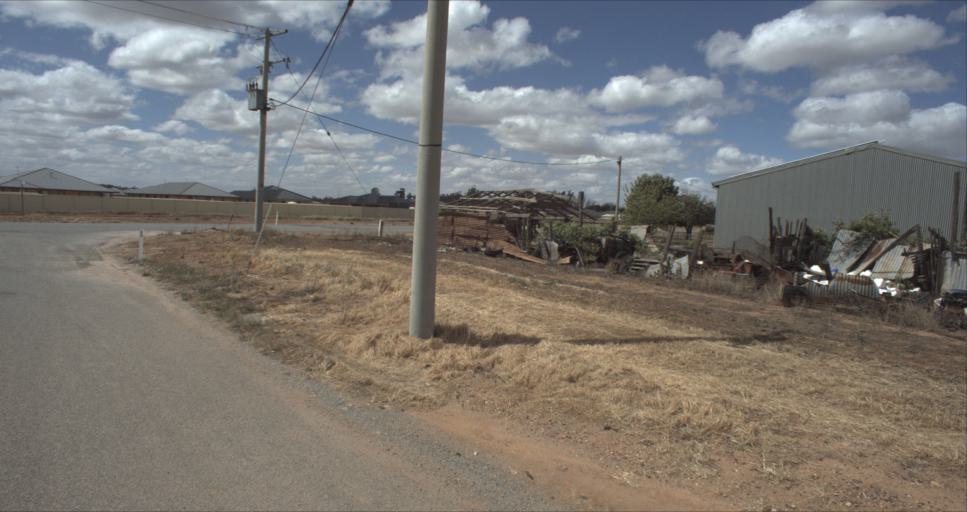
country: AU
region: New South Wales
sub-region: Leeton
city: Leeton
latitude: -34.5716
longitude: 146.3990
